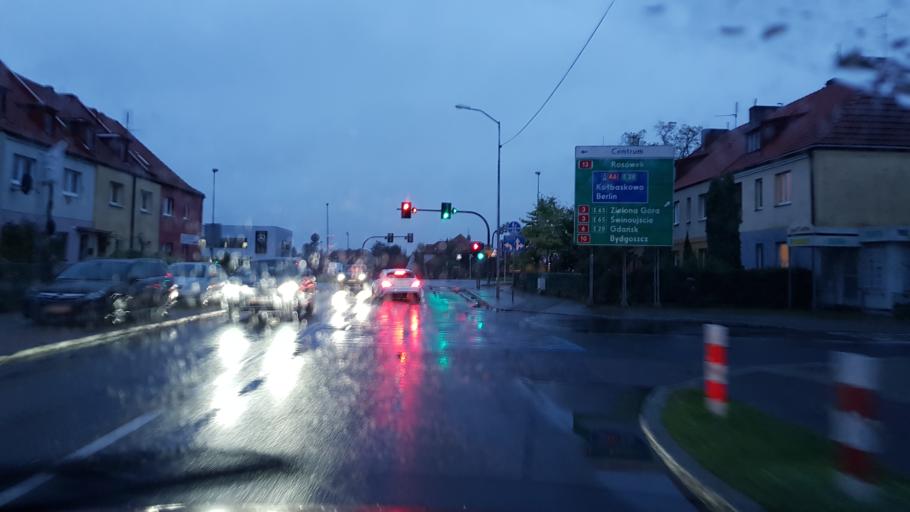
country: PL
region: West Pomeranian Voivodeship
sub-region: Powiat policki
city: Przeclaw
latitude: 53.4074
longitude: 14.5058
